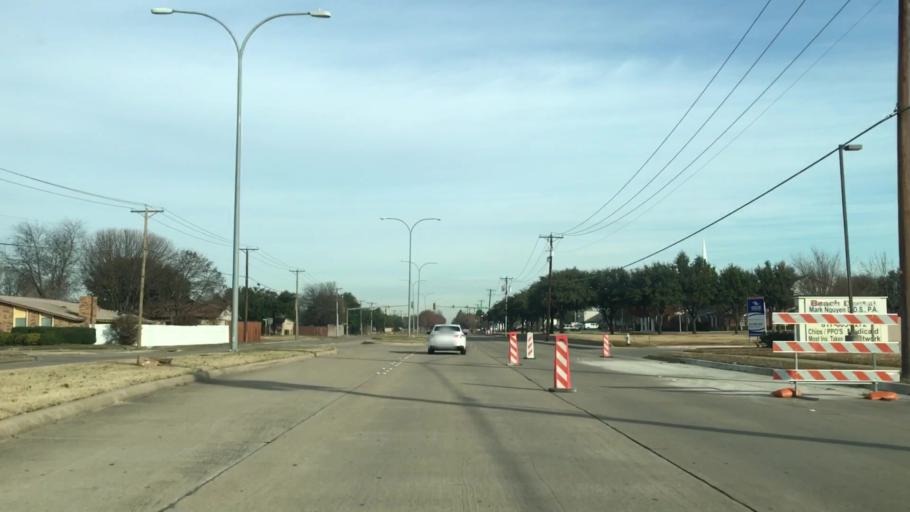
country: US
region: Texas
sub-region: Tarrant County
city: Watauga
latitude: 32.8759
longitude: -97.2896
